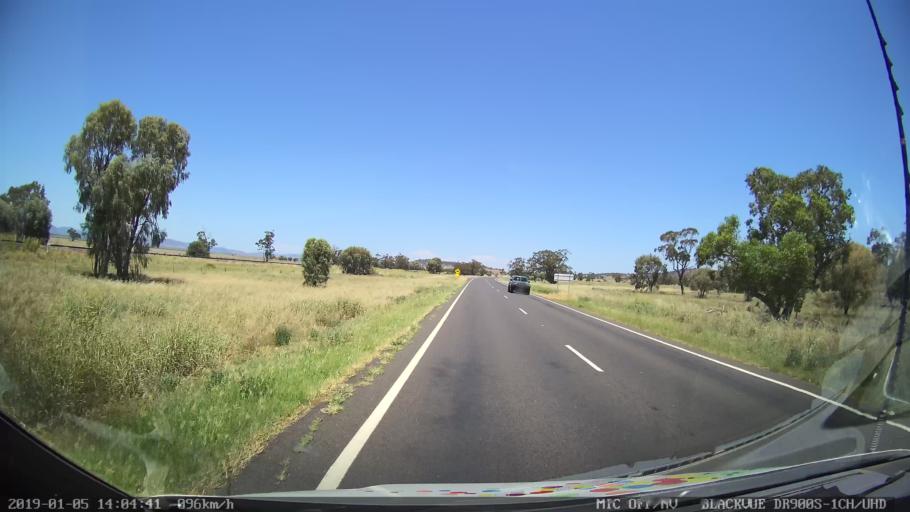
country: AU
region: New South Wales
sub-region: Gunnedah
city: Gunnedah
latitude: -31.2023
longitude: 150.3668
